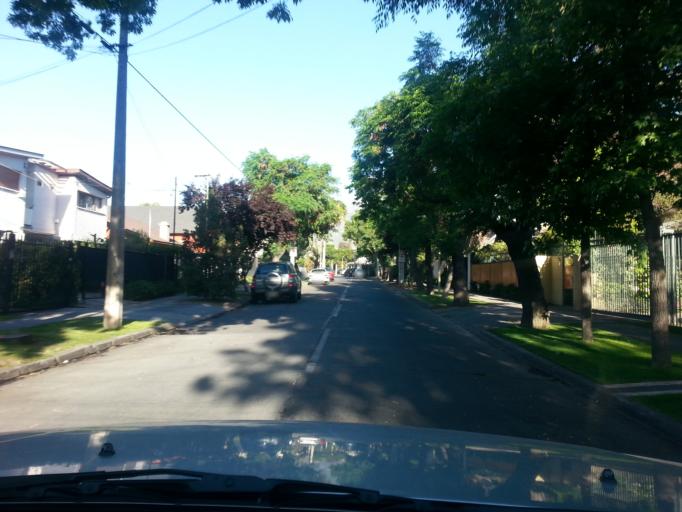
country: CL
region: Santiago Metropolitan
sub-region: Provincia de Santiago
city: Villa Presidente Frei, Nunoa, Santiago, Chile
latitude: -33.4286
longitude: -70.5719
